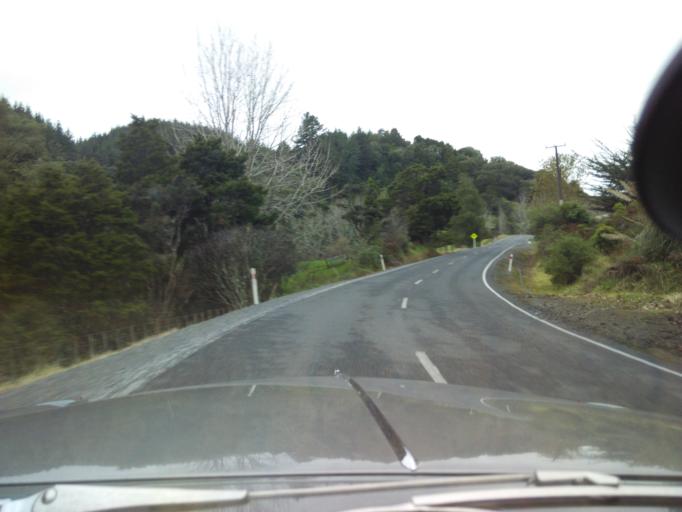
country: NZ
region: Auckland
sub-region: Auckland
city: Warkworth
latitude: -36.5028
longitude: 174.6415
